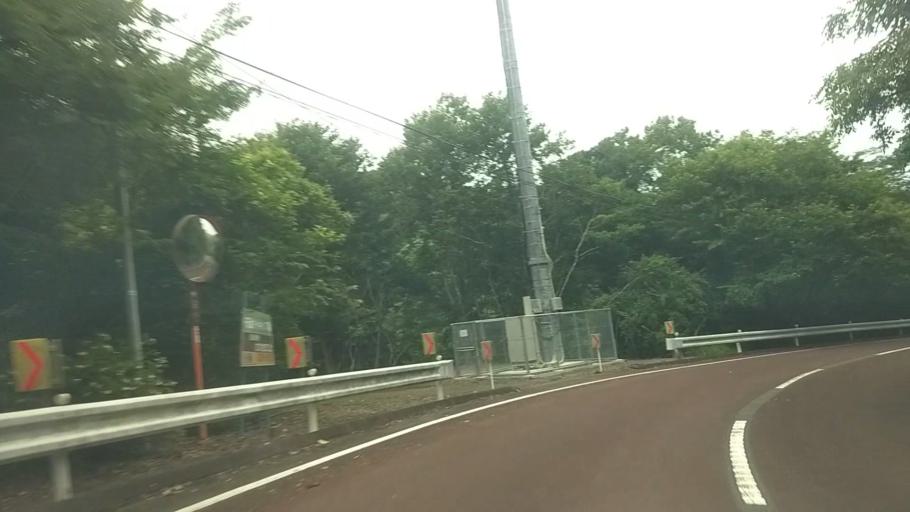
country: JP
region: Chiba
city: Kawaguchi
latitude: 35.1921
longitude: 140.1382
